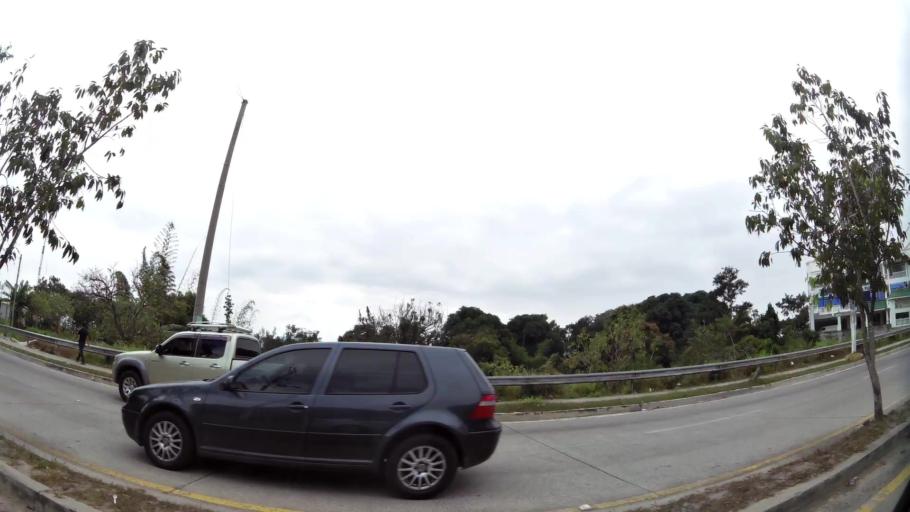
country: SV
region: San Salvador
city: Mejicanos
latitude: 13.7225
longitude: -89.2354
